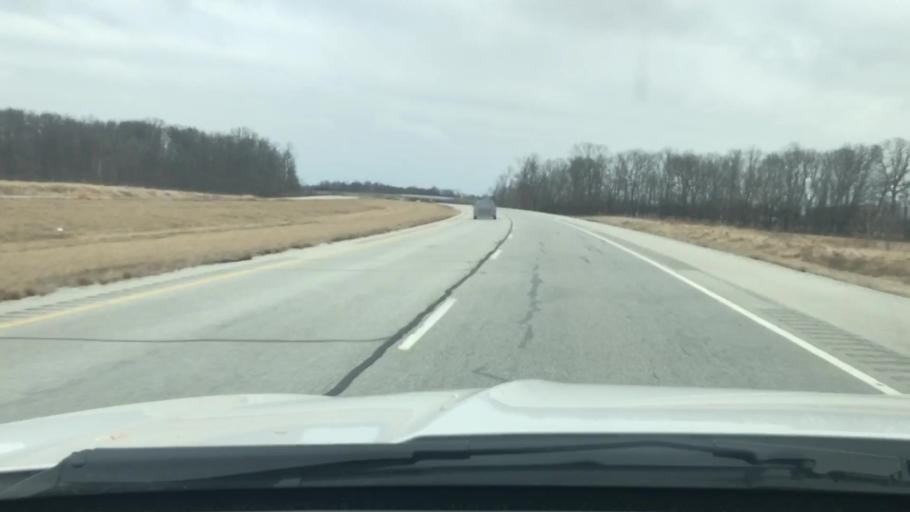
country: US
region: Indiana
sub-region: Carroll County
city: Delphi
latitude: 40.6373
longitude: -86.5842
